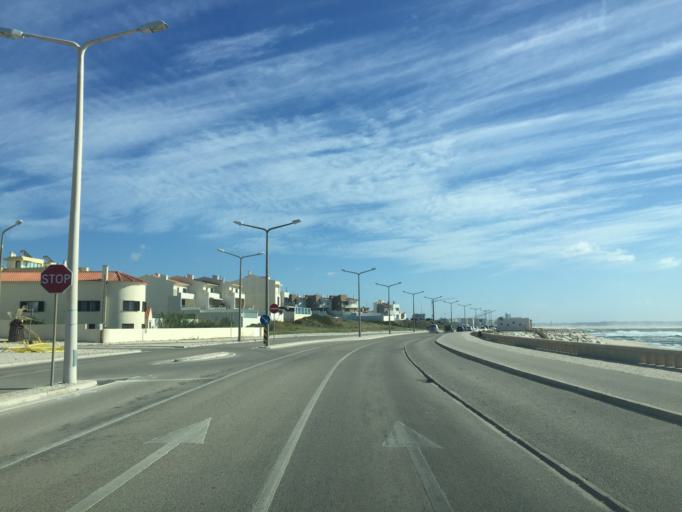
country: PT
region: Coimbra
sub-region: Figueira da Foz
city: Buarcos
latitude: 40.1706
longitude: -8.8897
